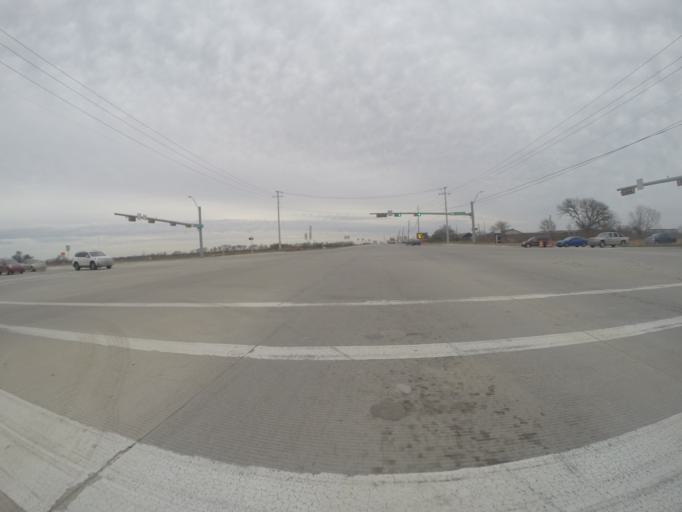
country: US
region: Texas
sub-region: Collin County
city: Wylie
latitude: 33.0082
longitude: -96.5733
